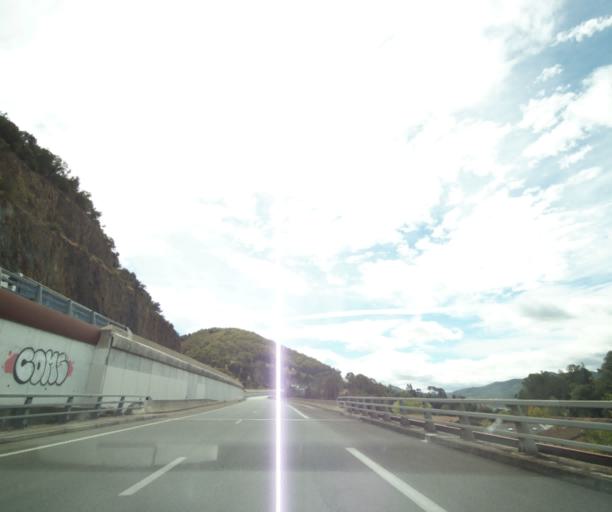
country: FR
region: Languedoc-Roussillon
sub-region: Departement de l'Herault
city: Lodeve
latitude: 43.7427
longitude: 3.3305
